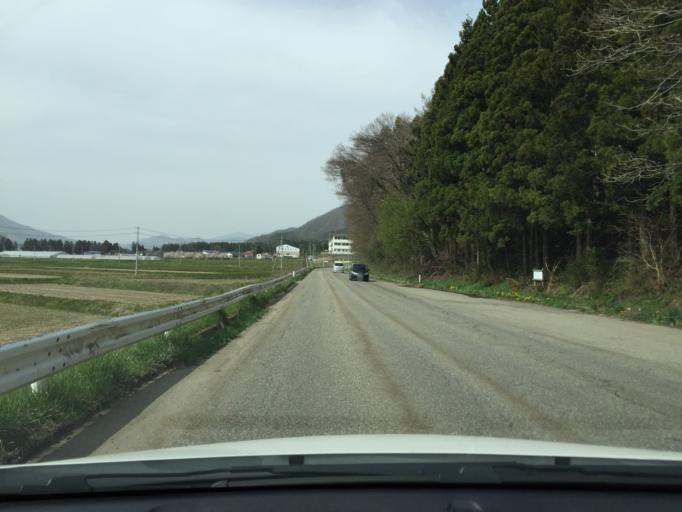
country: JP
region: Fukushima
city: Inawashiro
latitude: 37.5274
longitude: 140.1448
